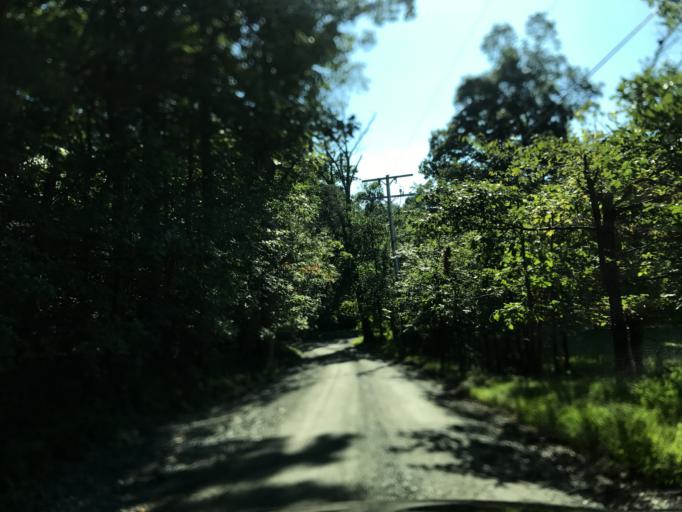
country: US
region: Pennsylvania
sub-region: York County
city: Stewartstown
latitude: 39.6870
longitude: -76.5461
